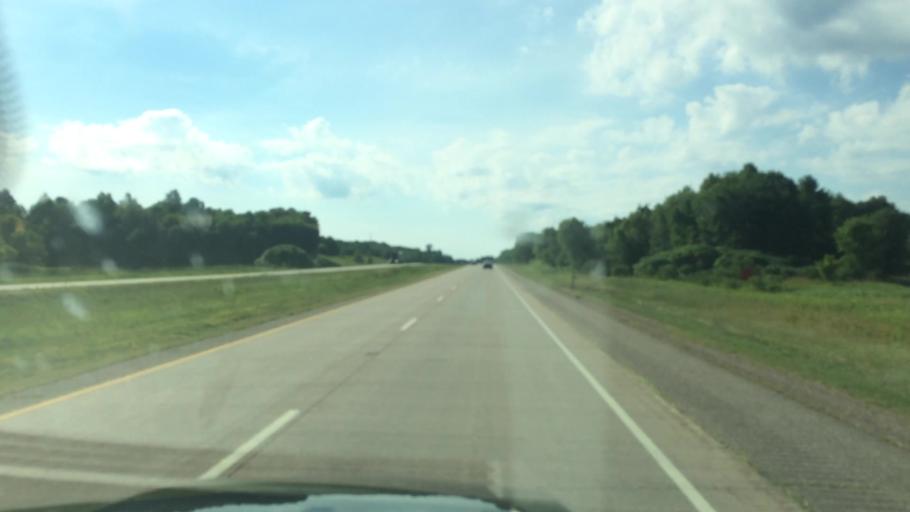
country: US
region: Wisconsin
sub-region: Shawano County
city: Wittenberg
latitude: 44.8133
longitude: -89.0454
